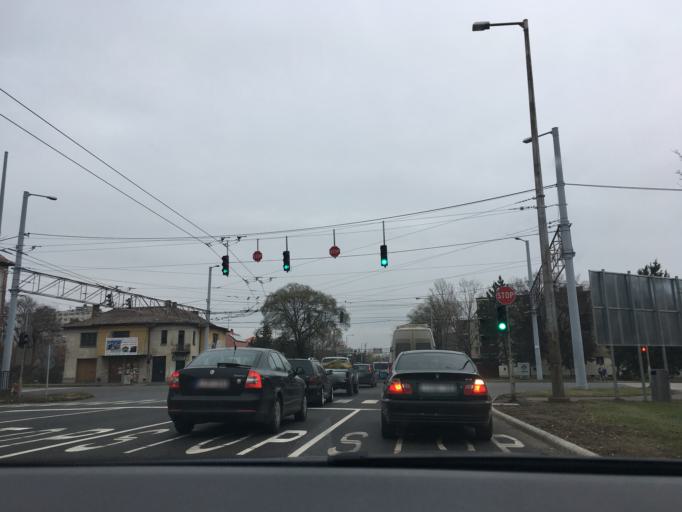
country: HU
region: Hajdu-Bihar
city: Debrecen
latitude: 47.5299
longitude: 21.6386
